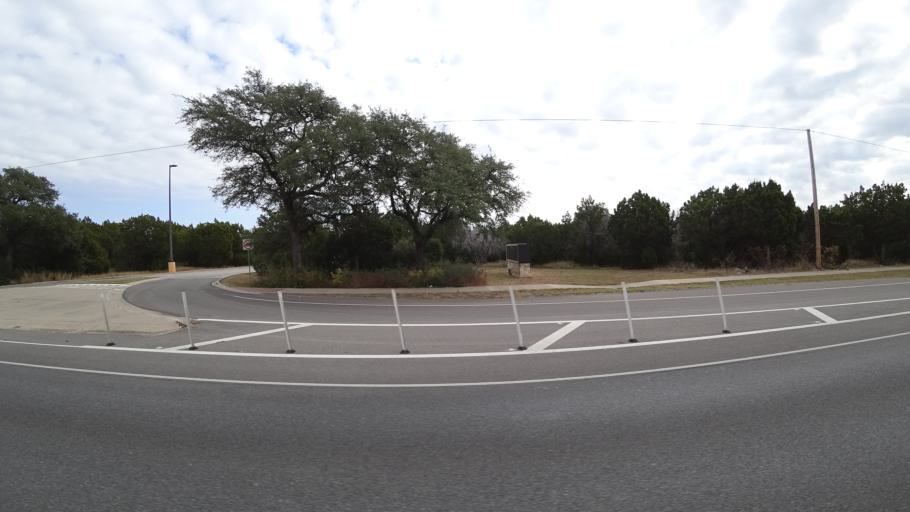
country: US
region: Texas
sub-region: Williamson County
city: Anderson Mill
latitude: 30.4178
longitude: -97.8468
